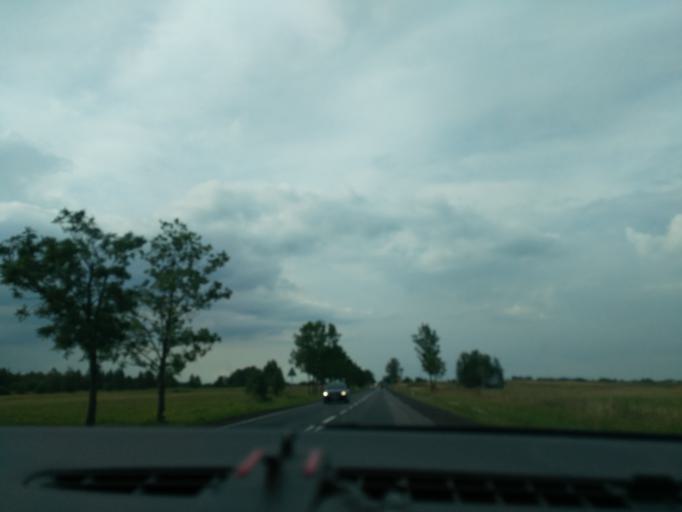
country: PL
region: Subcarpathian Voivodeship
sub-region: Powiat nizanski
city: Jezowe
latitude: 50.3592
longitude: 22.1231
